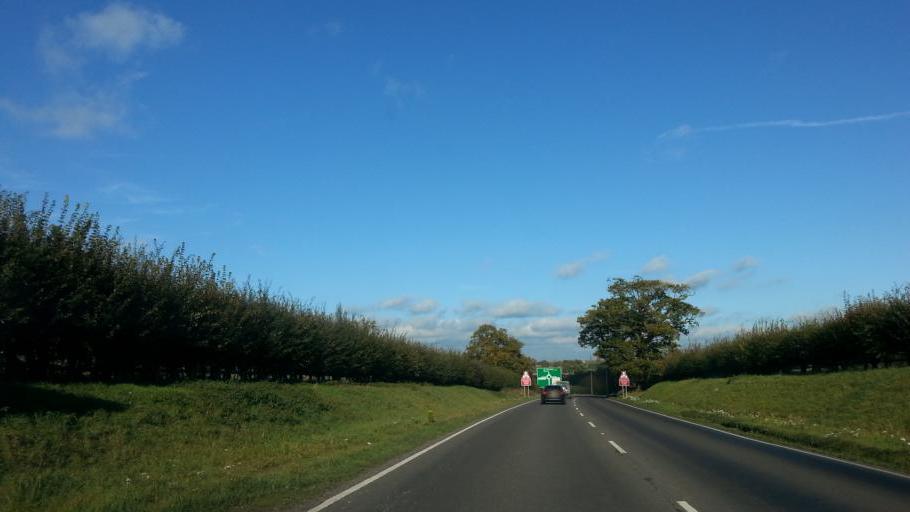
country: GB
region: England
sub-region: Norfolk
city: Harleston
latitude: 52.4077
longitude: 1.3175
